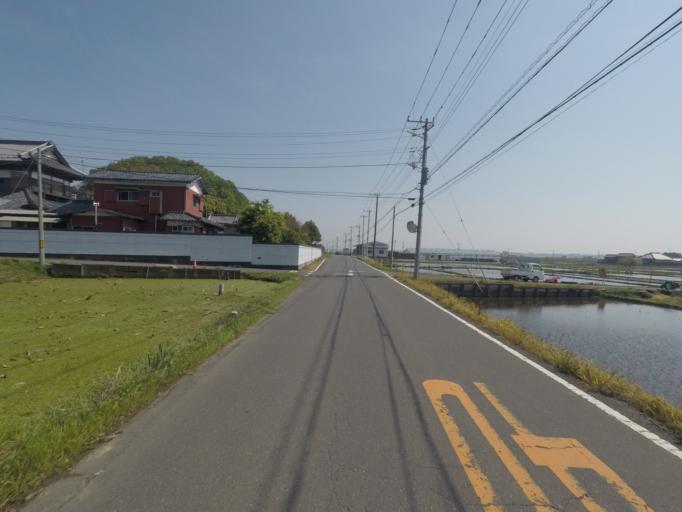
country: JP
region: Ibaraki
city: Ami
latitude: 36.0809
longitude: 140.2440
